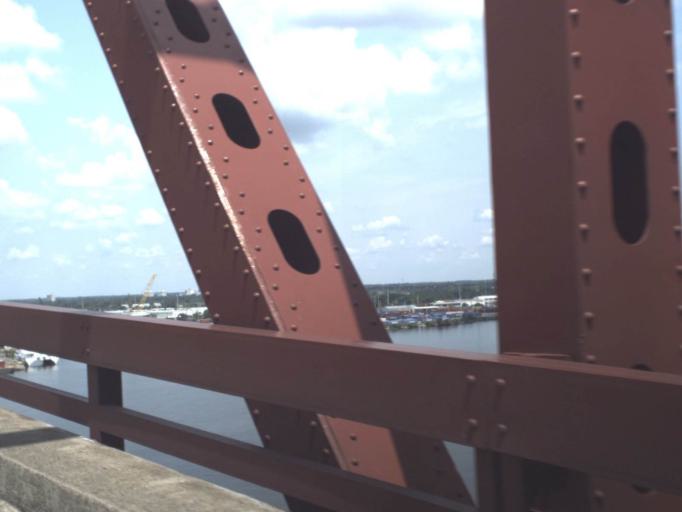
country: US
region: Florida
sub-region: Duval County
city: Jacksonville
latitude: 30.3273
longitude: -81.6204
